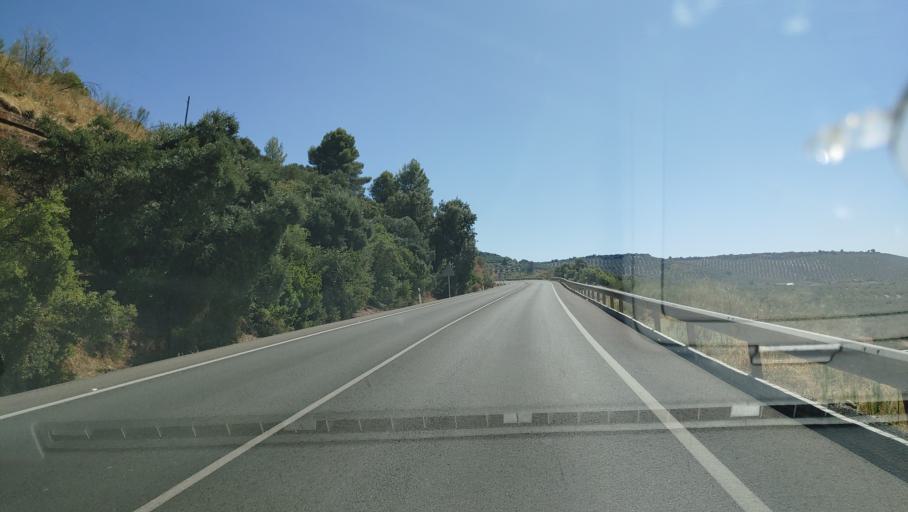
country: ES
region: Andalusia
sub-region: Provincia de Jaen
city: Campina
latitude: 38.2458
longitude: -2.9655
